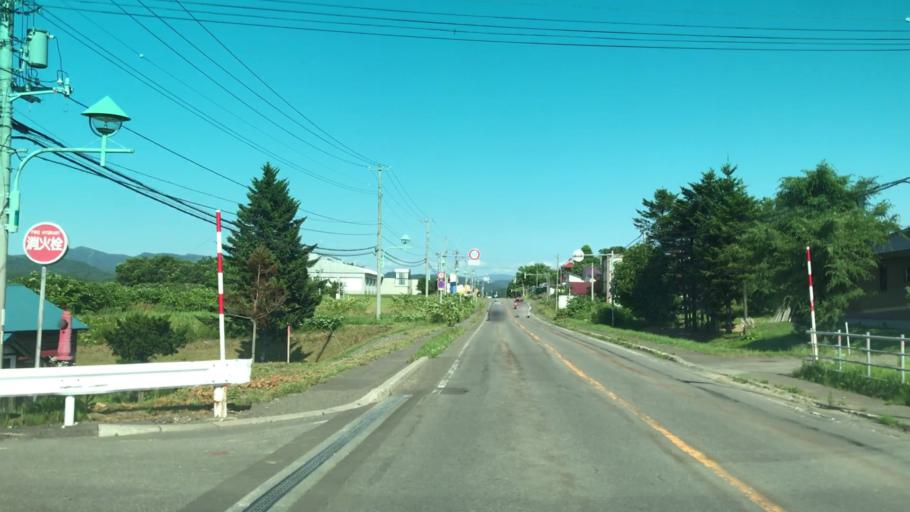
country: JP
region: Hokkaido
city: Iwanai
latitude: 42.9799
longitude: 140.6024
